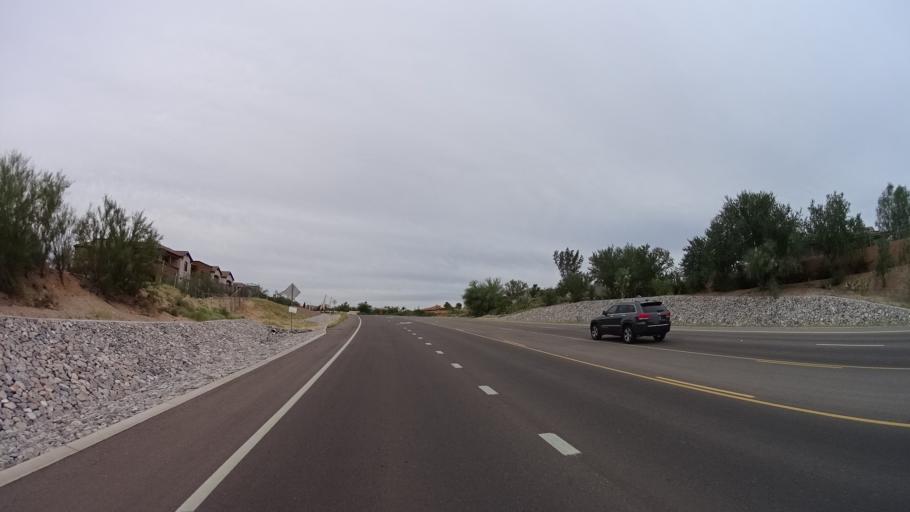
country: US
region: Arizona
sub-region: Pima County
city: Casas Adobes
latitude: 32.3560
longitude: -111.0308
